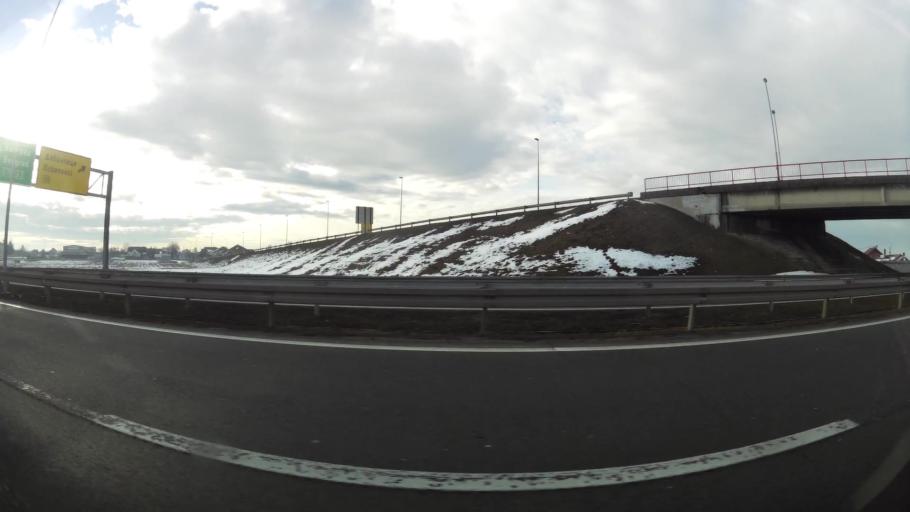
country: RS
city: Dobanovci
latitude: 44.8443
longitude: 20.2119
